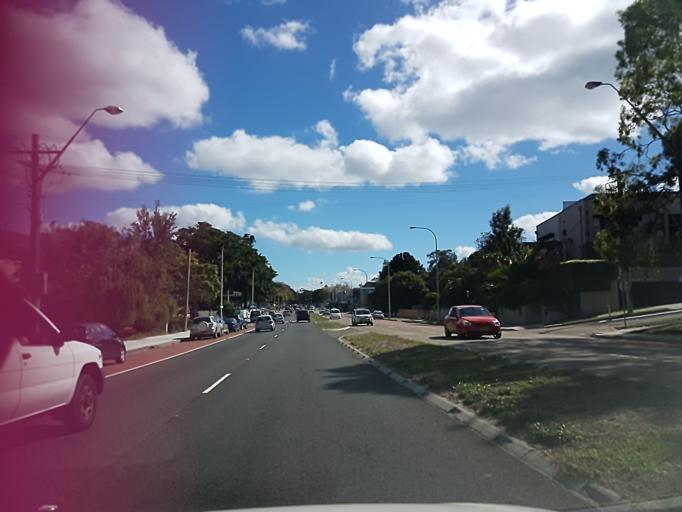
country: AU
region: New South Wales
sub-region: Warringah
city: Narrabeen
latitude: -33.7158
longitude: 151.2974
